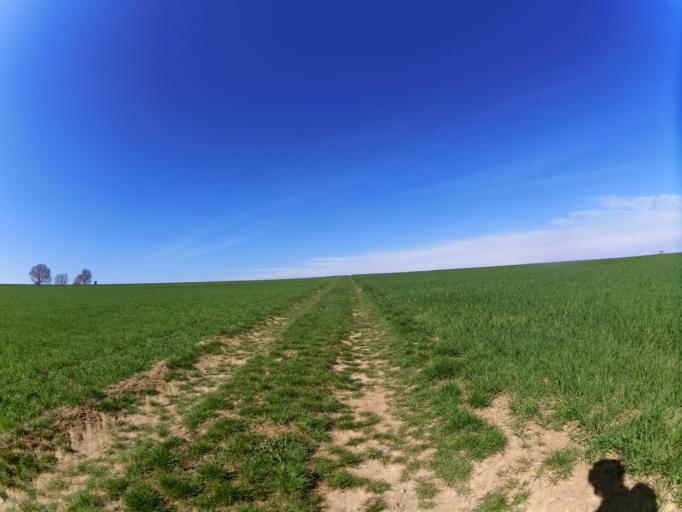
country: DE
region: Bavaria
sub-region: Regierungsbezirk Unterfranken
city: Winterhausen
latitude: 49.6829
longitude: 10.0011
